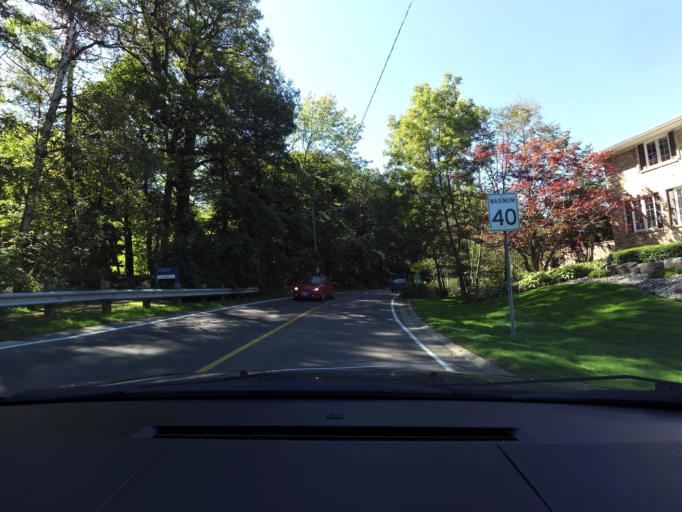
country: CA
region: Ontario
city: Hamilton
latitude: 43.3048
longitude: -79.8407
